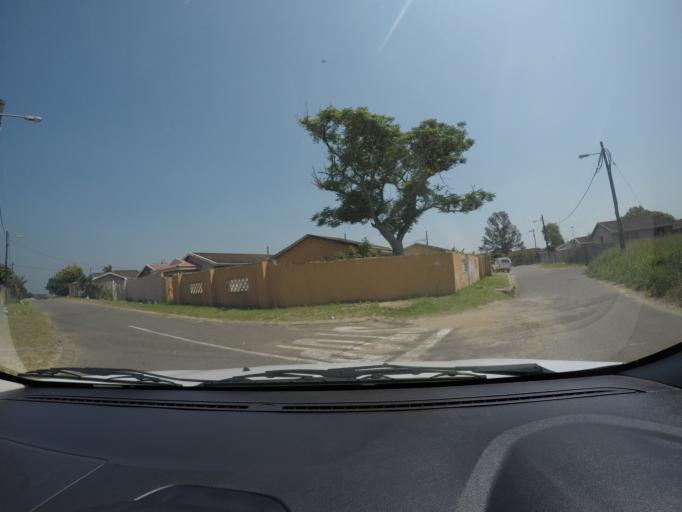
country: ZA
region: KwaZulu-Natal
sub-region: uThungulu District Municipality
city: eSikhawini
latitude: -28.8694
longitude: 31.9259
